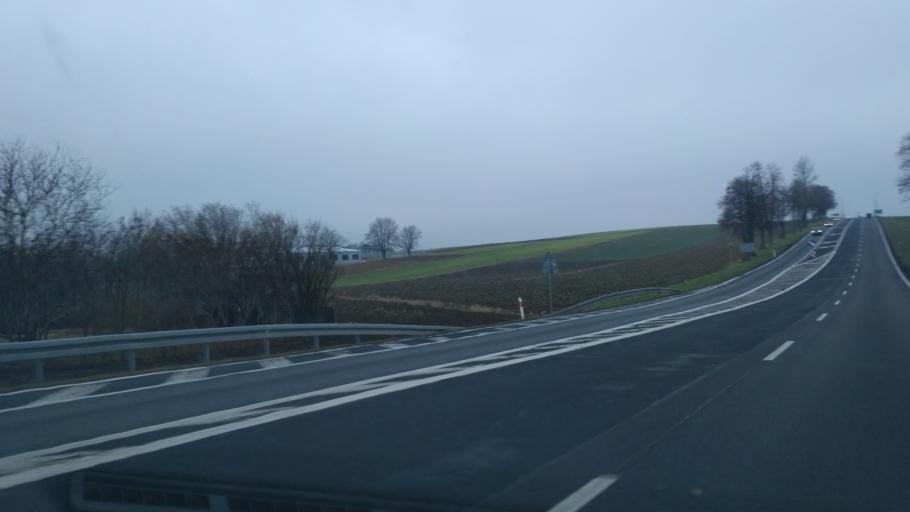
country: PL
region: Subcarpathian Voivodeship
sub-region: Powiat jaroslawski
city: Wierzbna
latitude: 50.0338
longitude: 22.5963
